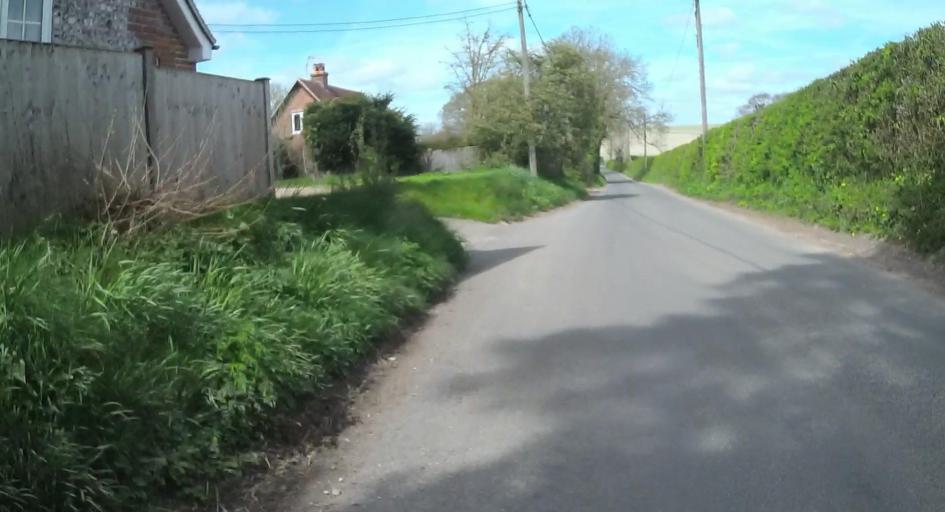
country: GB
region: England
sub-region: Hampshire
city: Romsey
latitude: 51.0790
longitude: -1.4583
